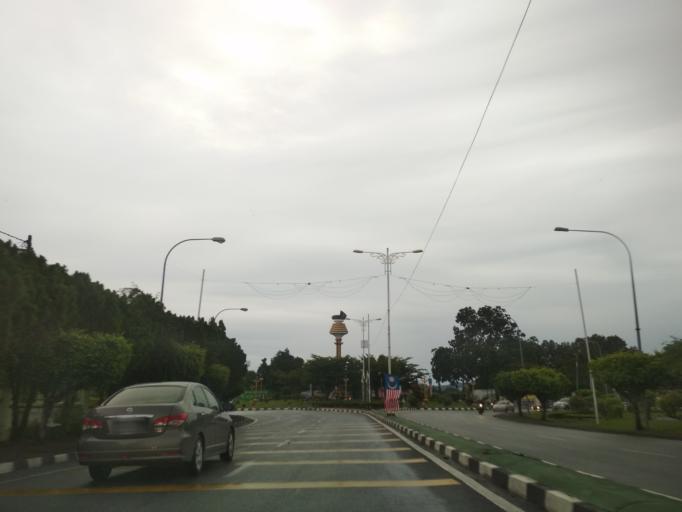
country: MY
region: Perlis
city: Kangar
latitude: 6.4440
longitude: 100.2053
